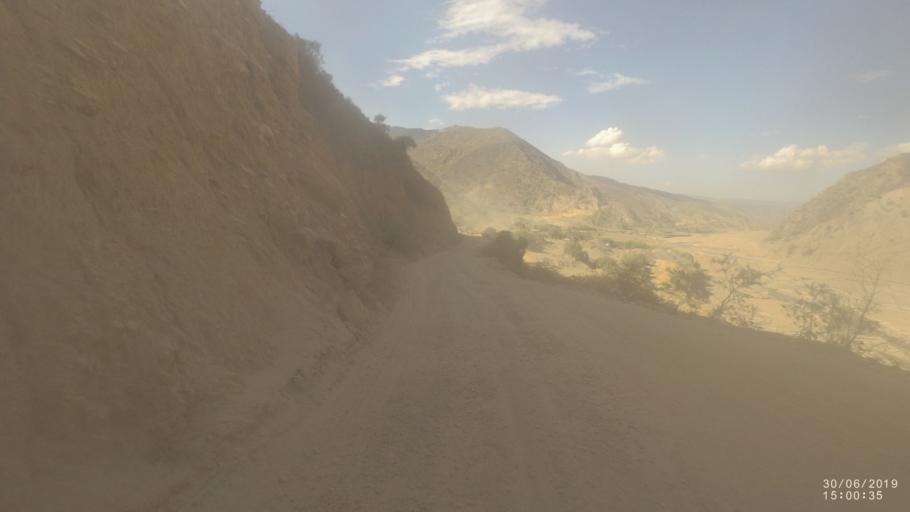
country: BO
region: Cochabamba
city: Irpa Irpa
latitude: -17.7360
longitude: -66.3405
